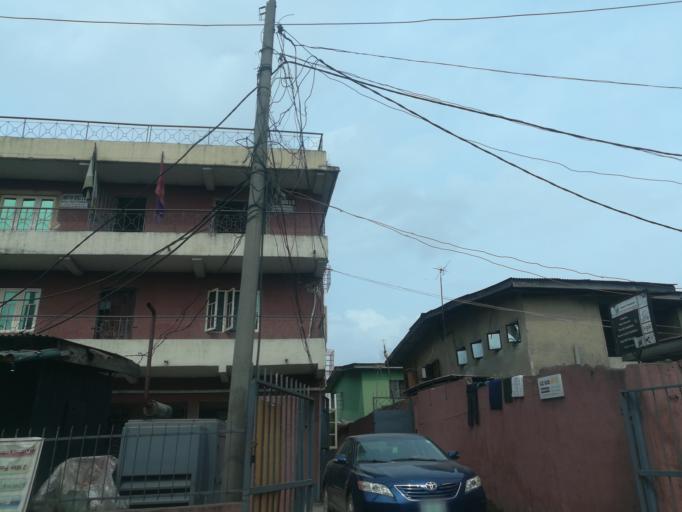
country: NG
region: Lagos
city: Ikeja
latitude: 6.5985
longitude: 3.3354
